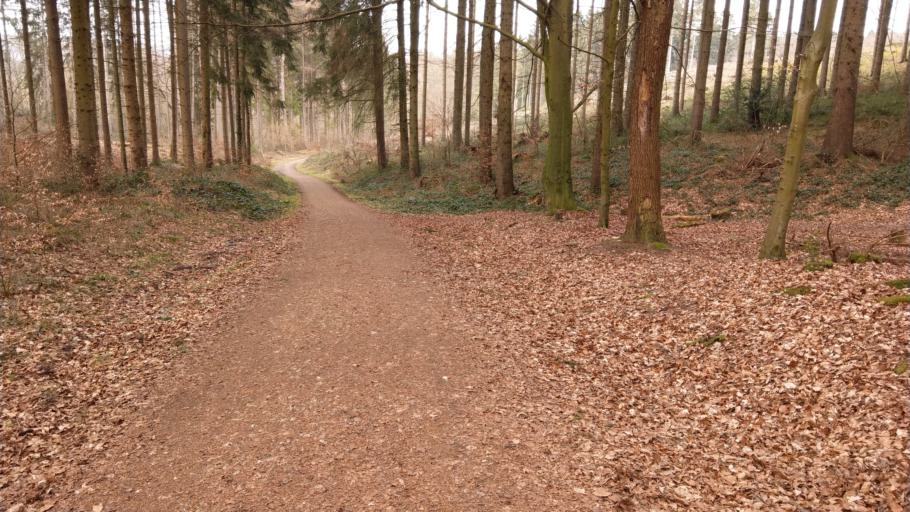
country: BE
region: Wallonia
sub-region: Province de Liege
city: La Calamine
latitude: 50.7295
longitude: 6.0468
